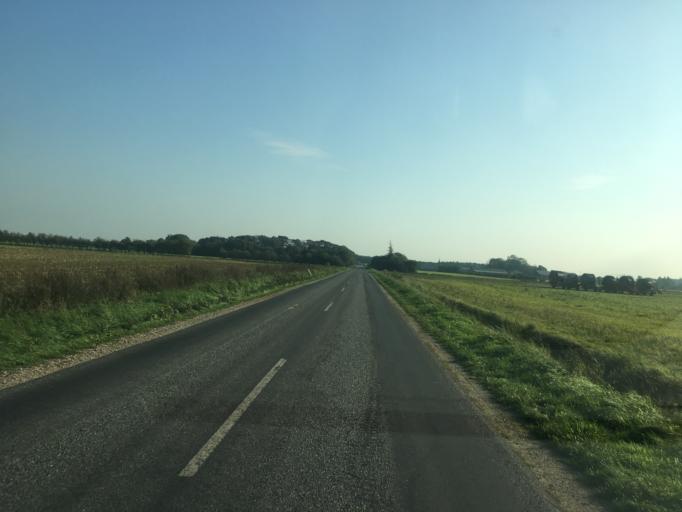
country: DE
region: Schleswig-Holstein
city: Bramstedtlund
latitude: 54.9373
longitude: 9.0669
